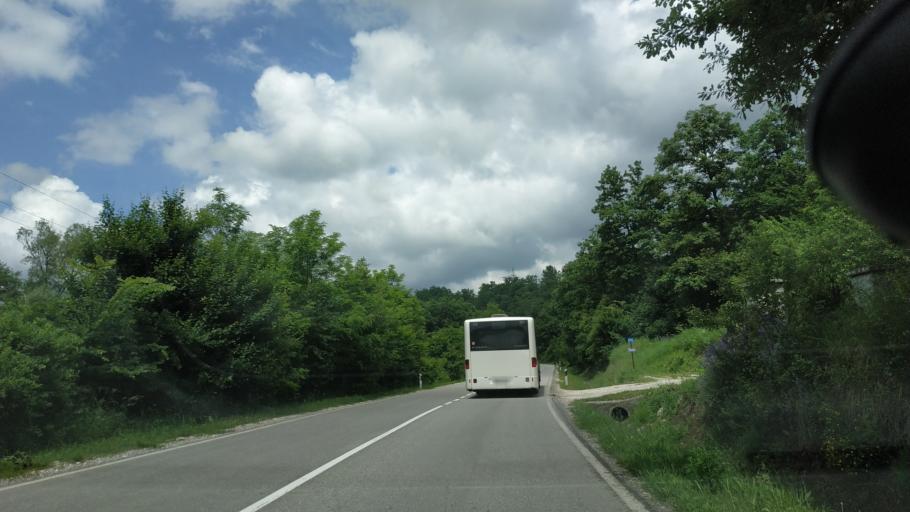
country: RS
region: Central Serbia
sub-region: Borski Okrug
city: Bor
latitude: 44.0549
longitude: 22.0695
